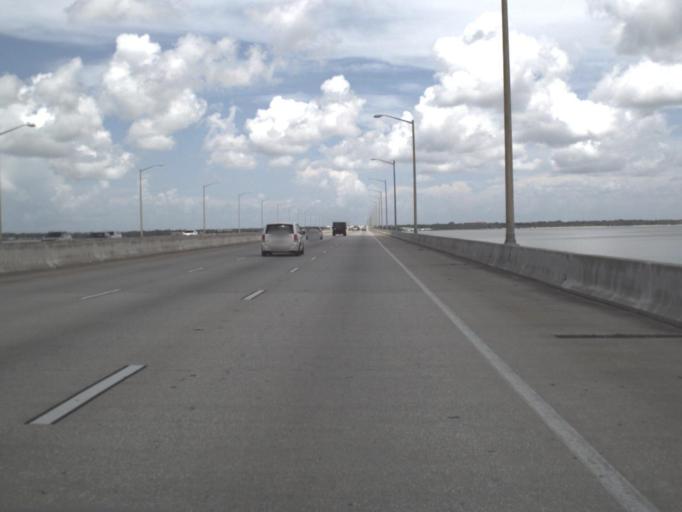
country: US
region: Florida
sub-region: Pinellas County
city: South Highpoint
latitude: 27.9281
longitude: -82.6998
